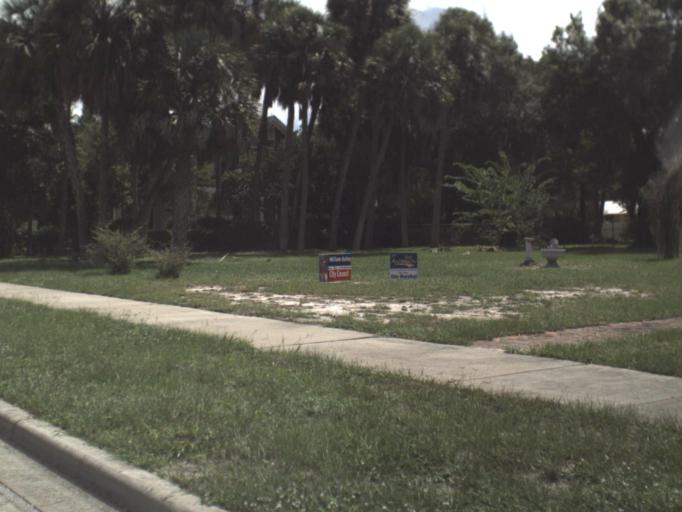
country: US
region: Florida
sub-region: DeSoto County
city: Arcadia
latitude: 27.2124
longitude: -81.8551
